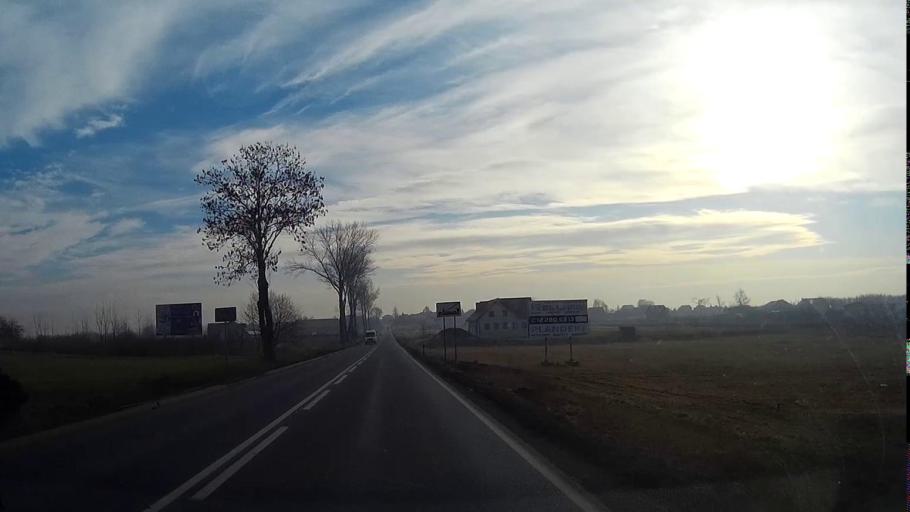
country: PL
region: Lesser Poland Voivodeship
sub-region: Powiat krakowski
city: Liszki
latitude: 50.0365
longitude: 19.7475
